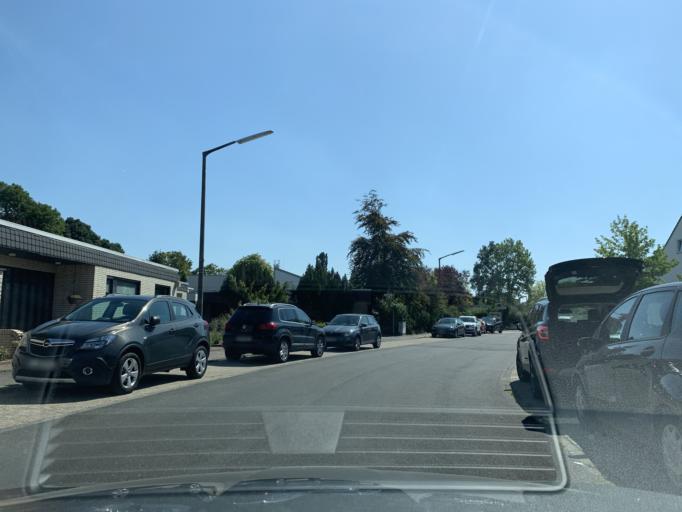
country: DE
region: North Rhine-Westphalia
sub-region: Regierungsbezirk Koln
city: Mengenich
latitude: 50.9996
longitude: 6.8720
